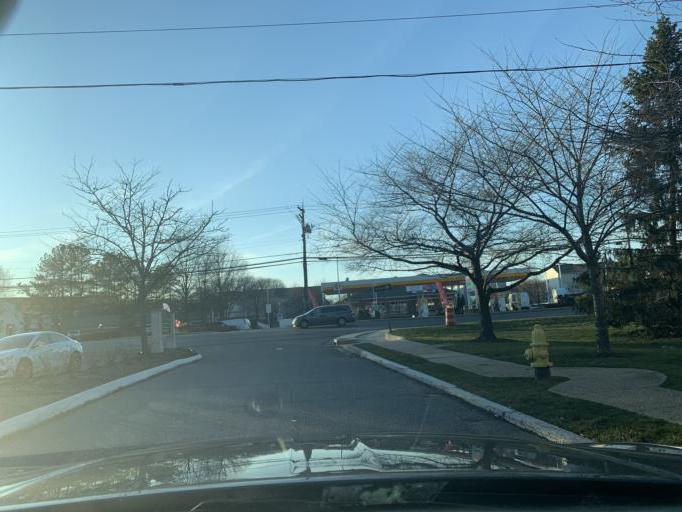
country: US
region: Maryland
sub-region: Anne Arundel County
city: Glen Burnie
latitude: 39.1511
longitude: -76.6314
